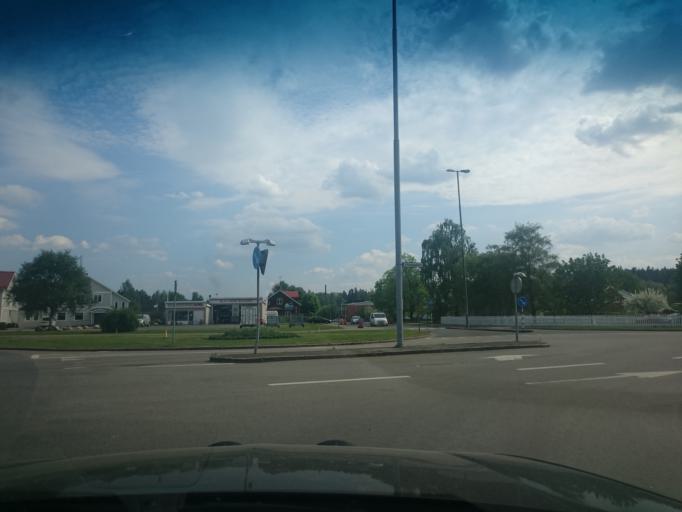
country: SE
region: Joenkoeping
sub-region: Vetlanda Kommun
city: Vetlanda
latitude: 57.4241
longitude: 15.0980
